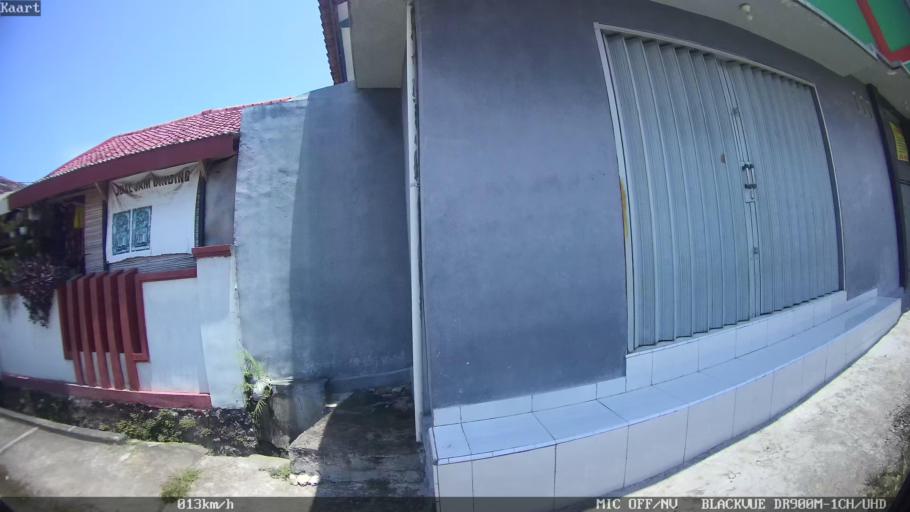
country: ID
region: Lampung
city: Kedaton
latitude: -5.3757
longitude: 105.2867
